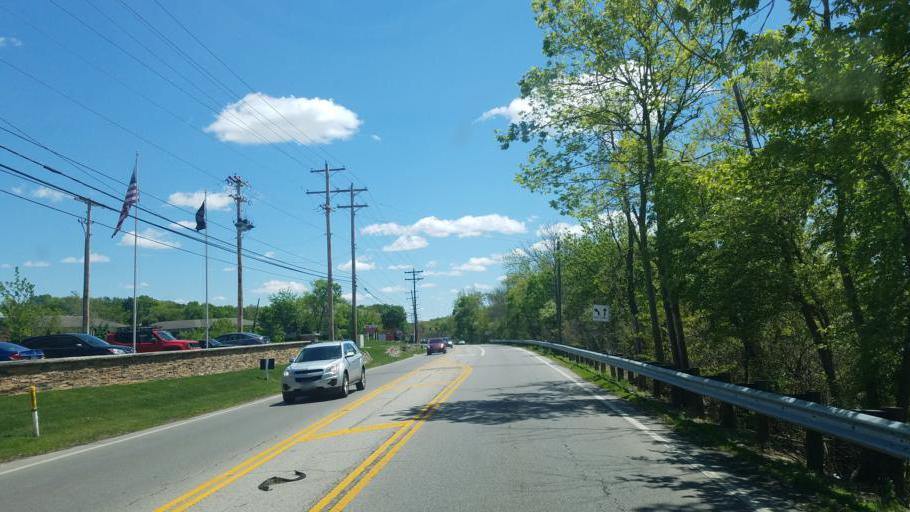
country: US
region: Ohio
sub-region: Franklin County
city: Dublin
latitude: 40.0638
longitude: -83.1039
